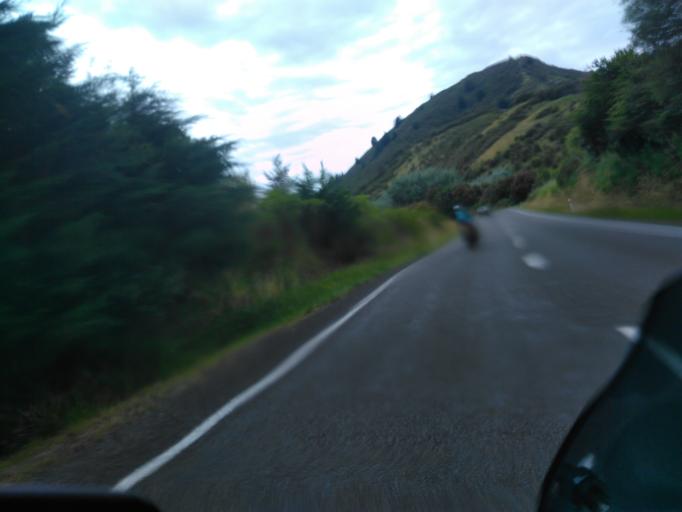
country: NZ
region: Gisborne
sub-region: Gisborne District
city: Gisborne
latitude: -38.4407
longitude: 177.5918
